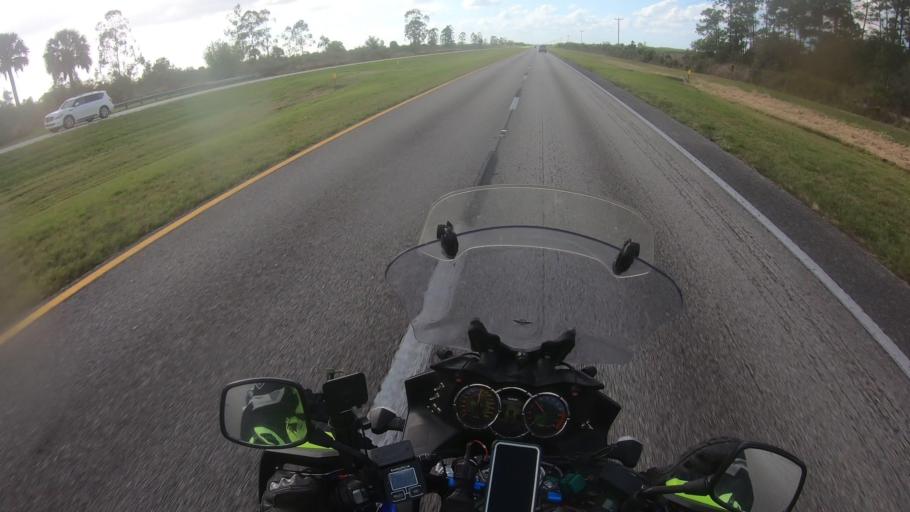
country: US
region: Florida
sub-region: Glades County
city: Moore Haven
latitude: 26.9037
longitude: -81.2586
